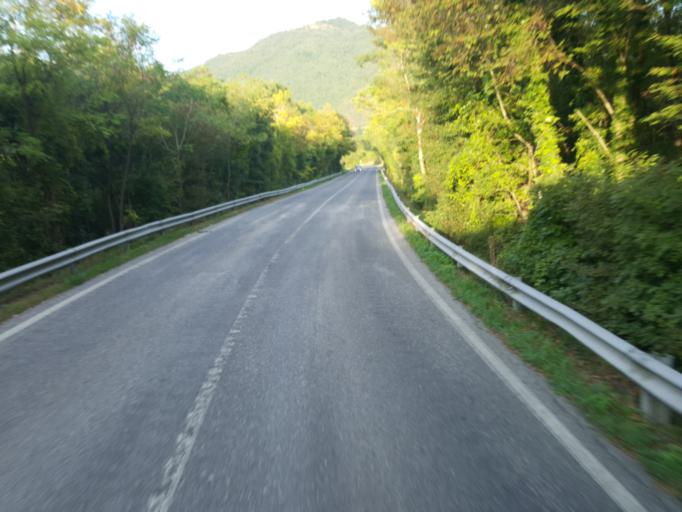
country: IT
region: Umbria
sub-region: Provincia di Perugia
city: Fossato di Vico
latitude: 43.3094
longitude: 12.8252
